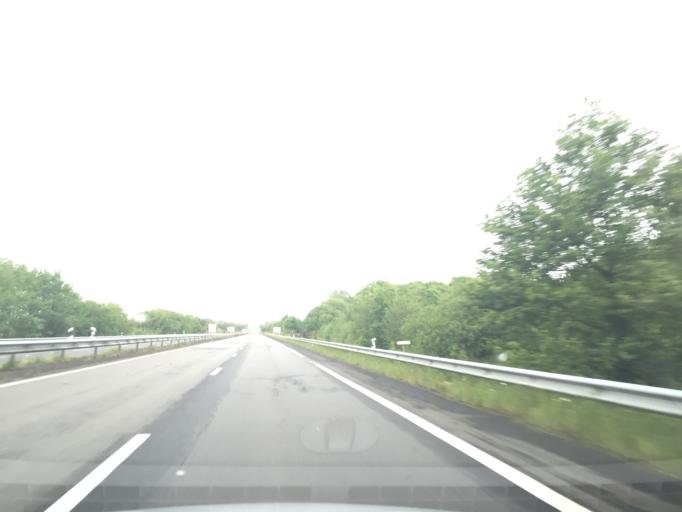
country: FR
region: Brittany
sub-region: Departement d'Ille-et-Vilaine
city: Roz-sur-Couesnon
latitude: 48.5668
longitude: -1.5853
